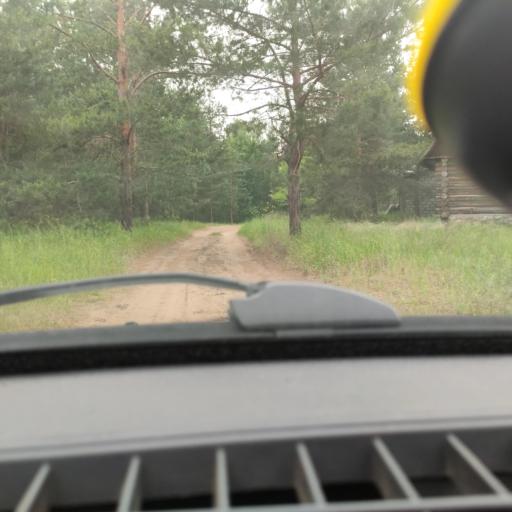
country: RU
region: Samara
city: Zhigulevsk
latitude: 53.5035
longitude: 49.5028
